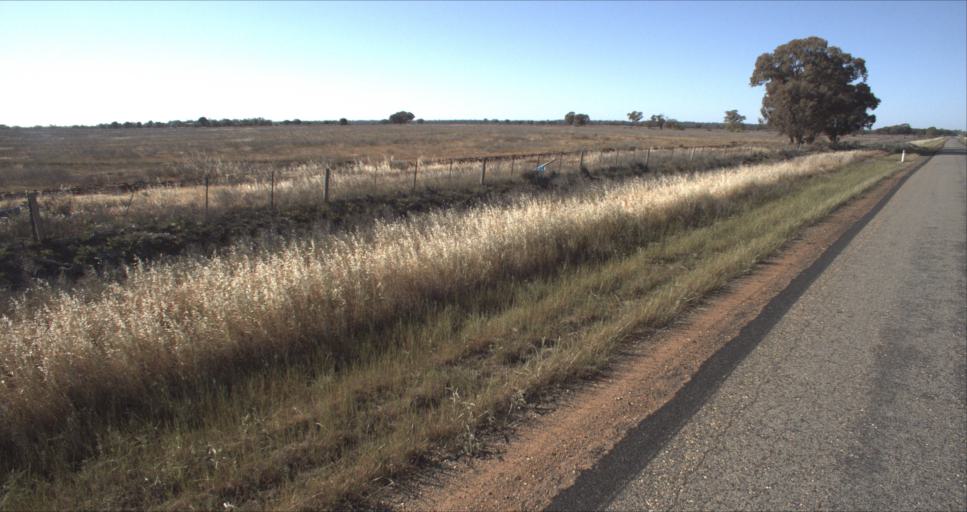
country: AU
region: New South Wales
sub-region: Leeton
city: Leeton
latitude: -34.5788
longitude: 146.2620
